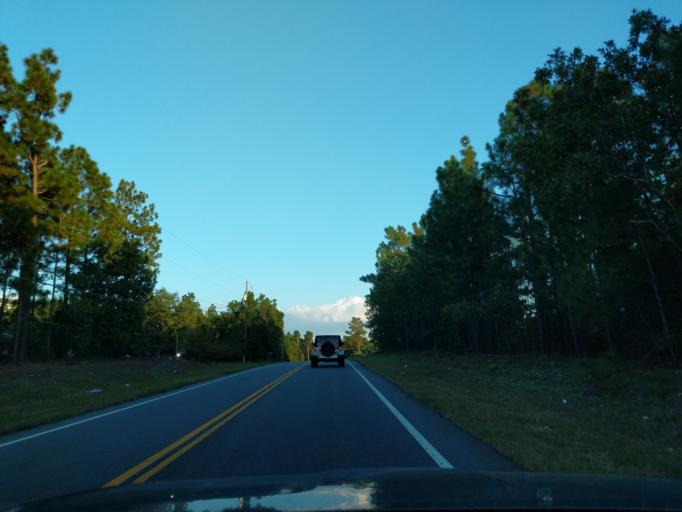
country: US
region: South Carolina
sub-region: Aiken County
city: Burnettown
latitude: 33.5386
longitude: -81.8675
